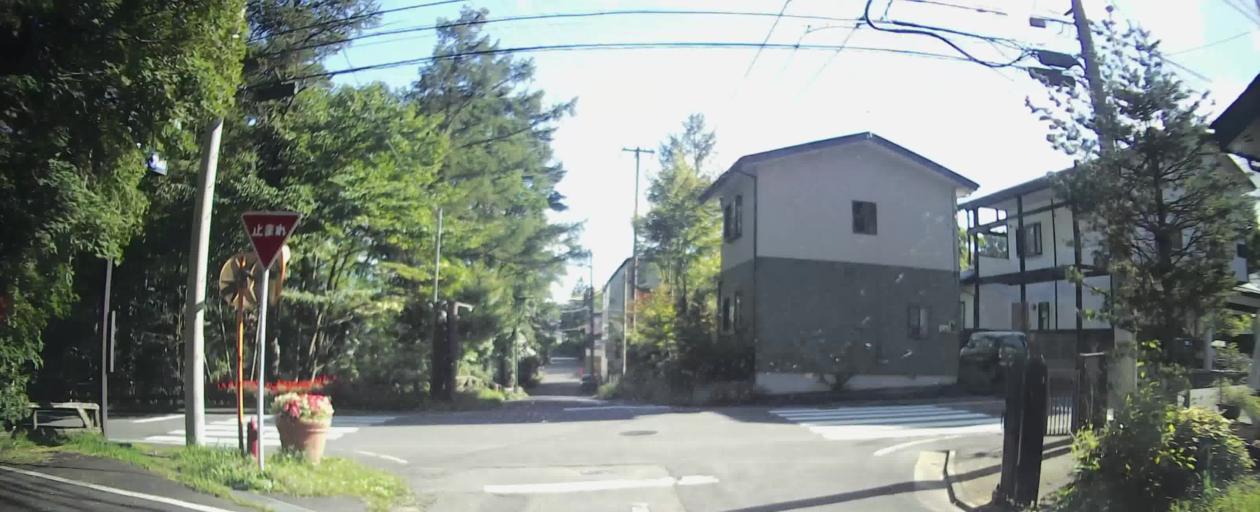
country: JP
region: Gunma
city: Nakanojomachi
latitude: 36.6275
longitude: 138.5996
